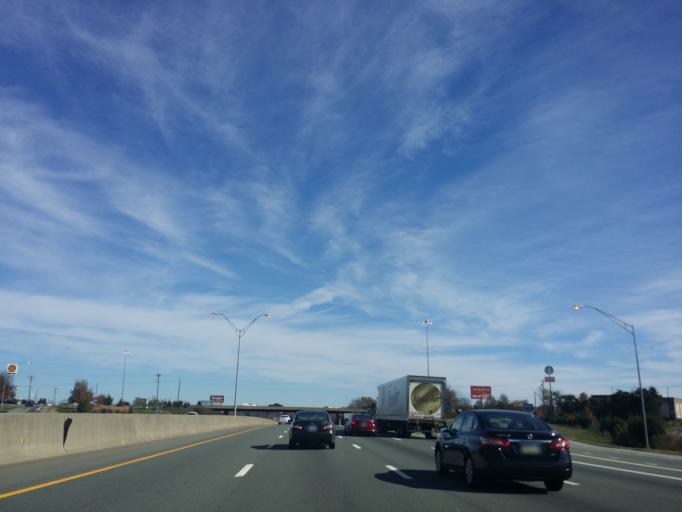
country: US
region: North Carolina
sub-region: Alamance County
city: Mebane
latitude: 36.0702
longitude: -79.2743
